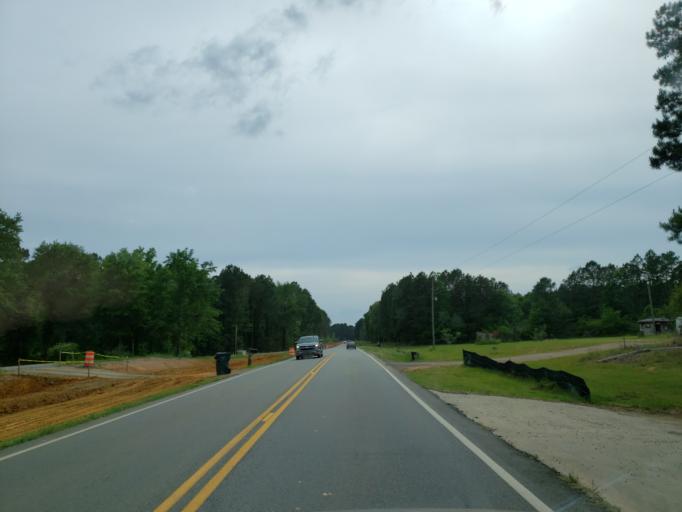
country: US
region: Georgia
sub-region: Macon County
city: Marshallville
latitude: 32.3833
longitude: -83.8759
